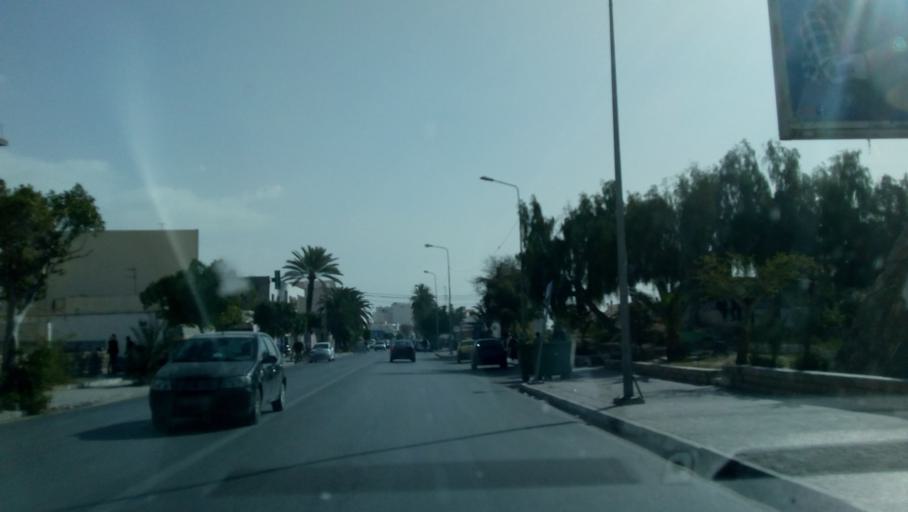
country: TN
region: Qabis
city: Gabes
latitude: 33.8849
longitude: 10.0934
